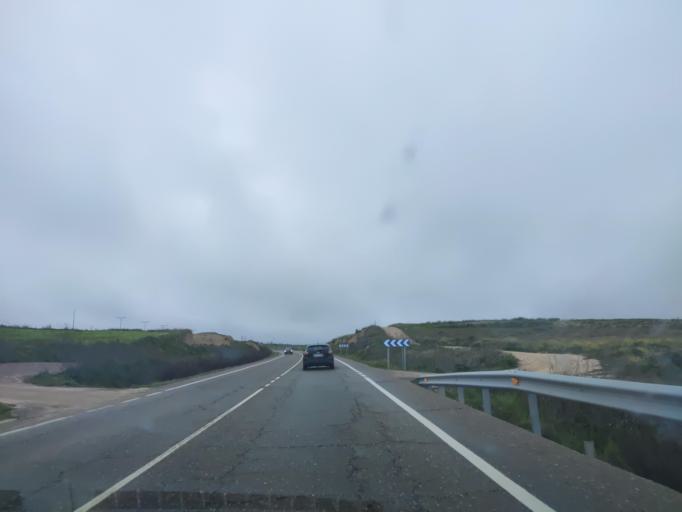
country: ES
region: Castille-La Mancha
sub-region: Province of Toledo
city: Bargas
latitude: 39.9459
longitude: -4.0253
